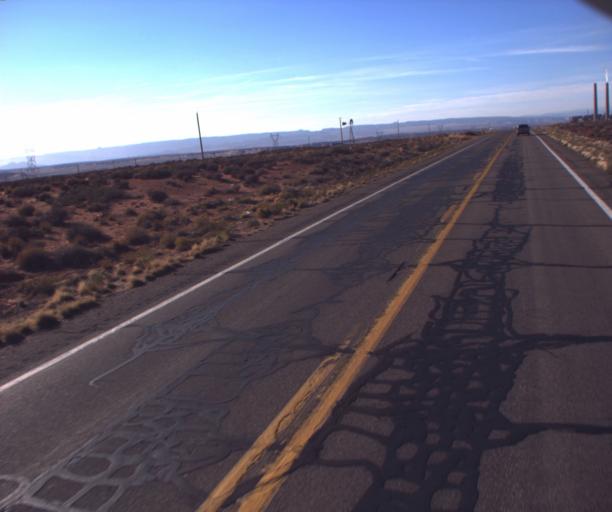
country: US
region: Arizona
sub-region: Coconino County
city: LeChee
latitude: 36.8843
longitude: -111.3564
